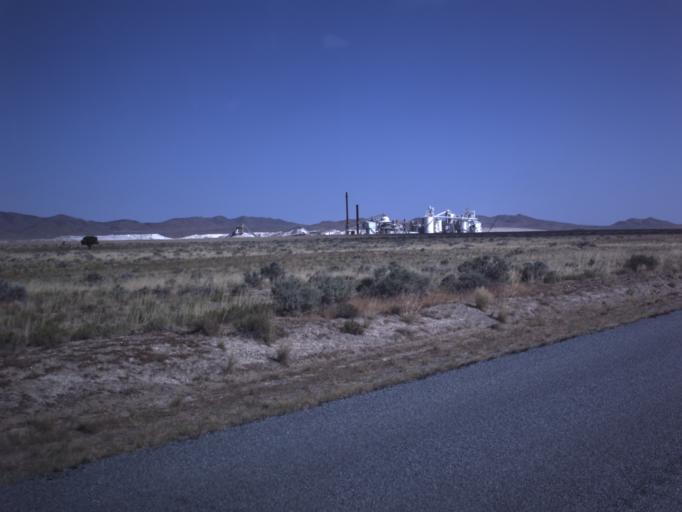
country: US
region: Utah
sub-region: Millard County
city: Delta
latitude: 38.9278
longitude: -112.8104
